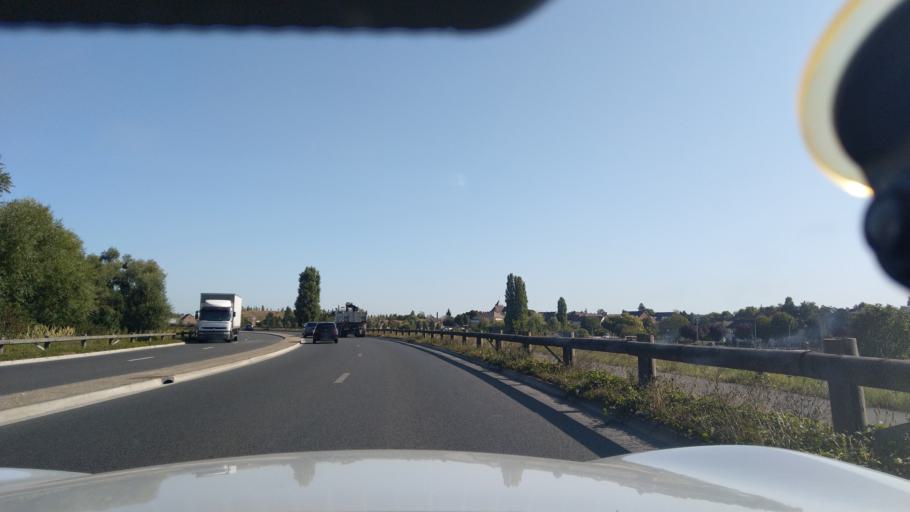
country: FR
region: Ile-de-France
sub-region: Departement du Val-d'Oise
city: Arnouville
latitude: 48.9717
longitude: 2.4245
